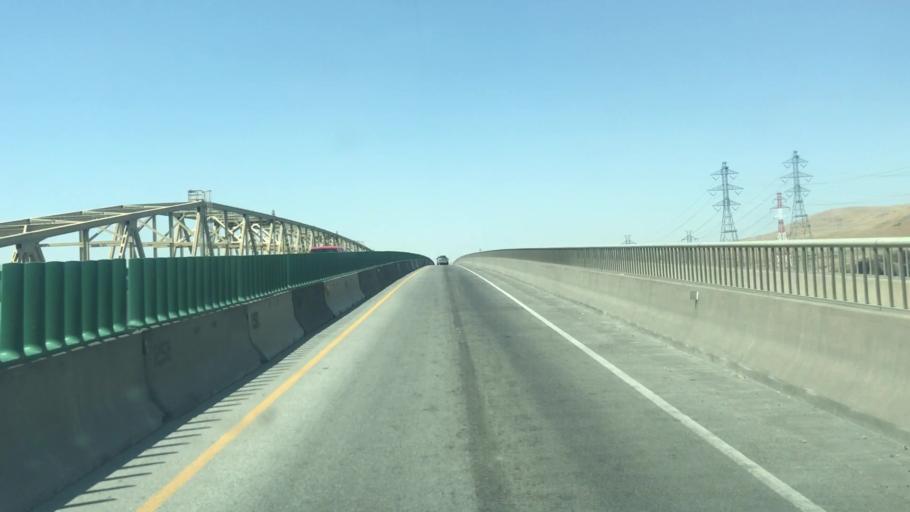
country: US
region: Oregon
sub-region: Umatilla County
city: Umatilla
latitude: 45.9282
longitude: -119.3266
